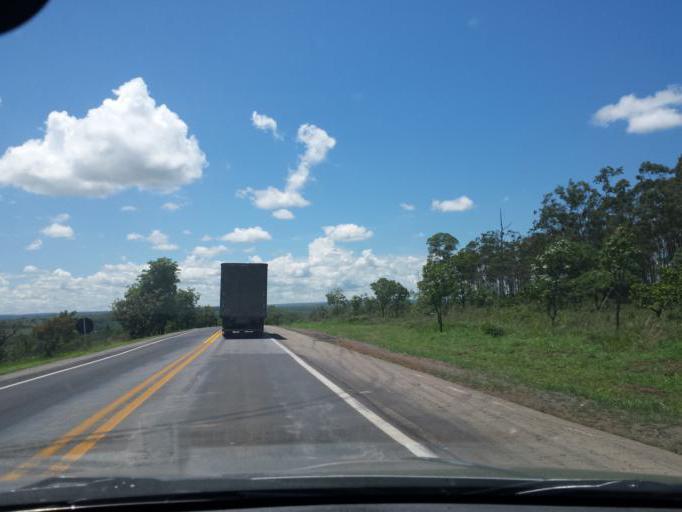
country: BR
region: Goias
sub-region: Luziania
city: Luziania
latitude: -16.5222
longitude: -47.8100
